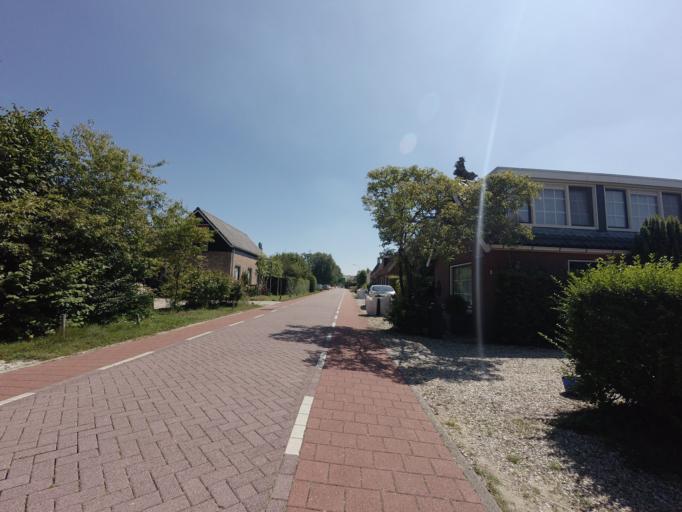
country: NL
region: Utrecht
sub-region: Stichtse Vecht
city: Maarssen
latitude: 52.1524
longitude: 5.0773
